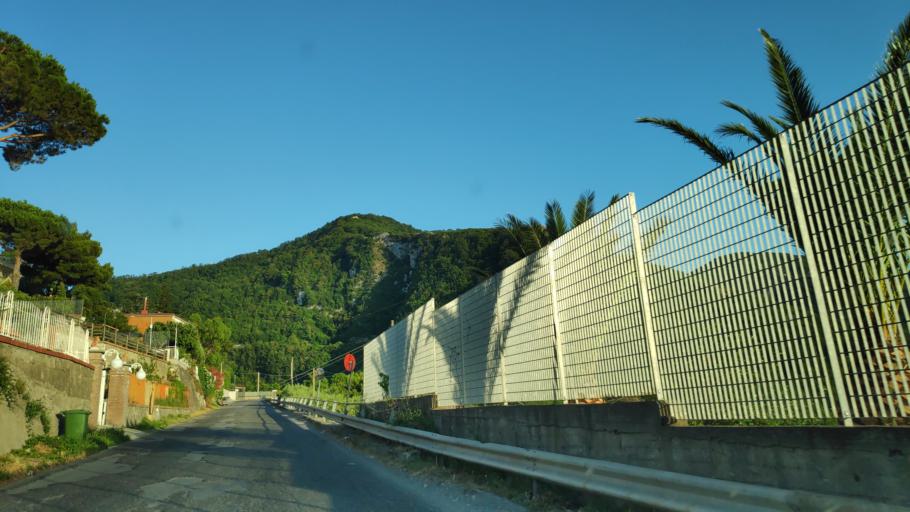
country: IT
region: Campania
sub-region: Provincia di Salerno
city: Corbara
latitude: 40.7237
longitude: 14.6037
